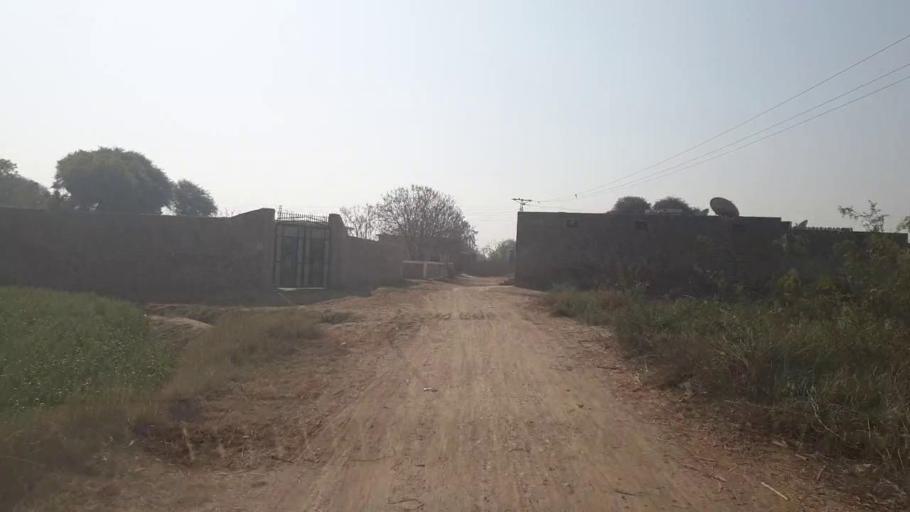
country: PK
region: Sindh
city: Tando Allahyar
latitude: 25.4595
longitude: 68.7822
